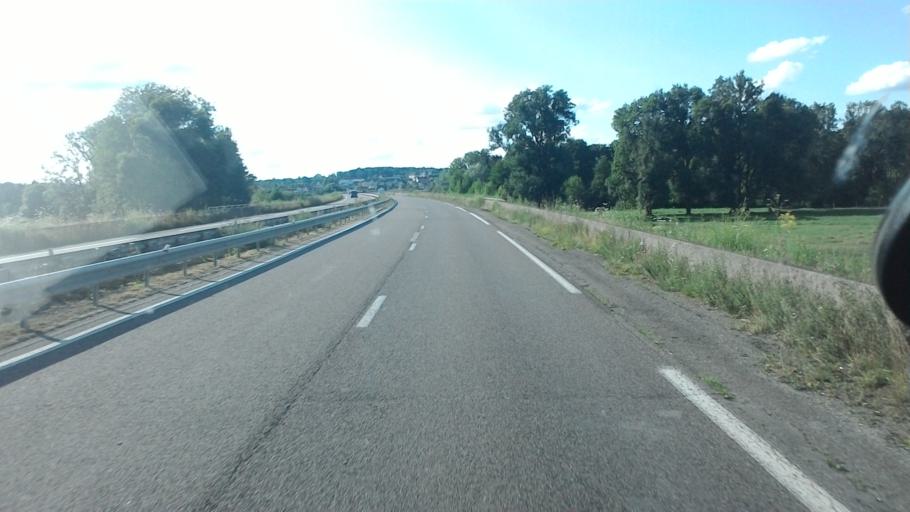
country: FR
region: Franche-Comte
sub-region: Departement de la Haute-Saone
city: Saint-Sauveur
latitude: 47.8110
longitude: 6.4016
